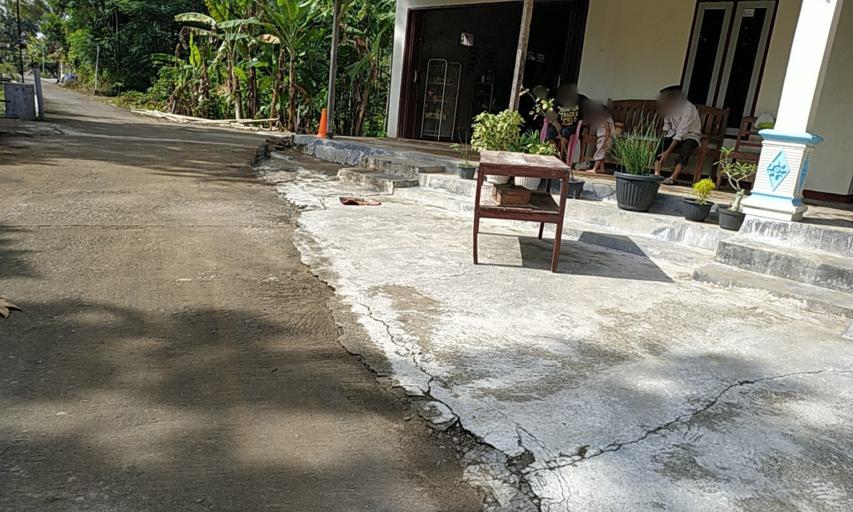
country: ID
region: Central Java
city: Trucuk
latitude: -7.7654
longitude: 110.6825
